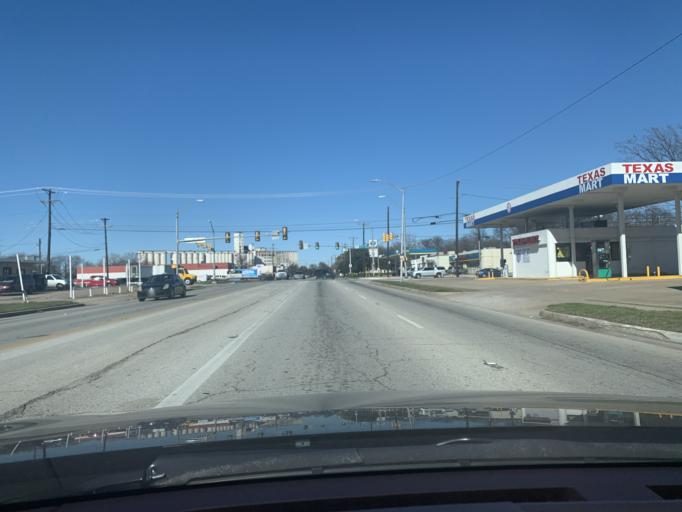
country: US
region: Texas
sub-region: Tarrant County
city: Haltom City
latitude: 32.7645
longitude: -97.2876
